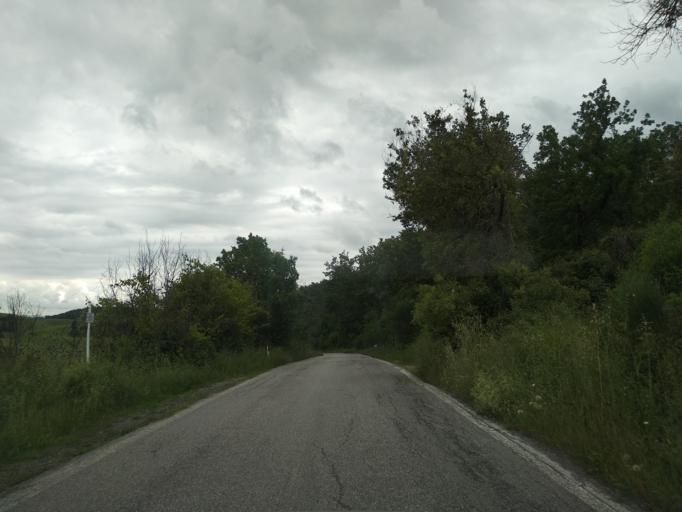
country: IT
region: Tuscany
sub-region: Provincia di Livorno
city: Guasticce
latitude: 43.5664
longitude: 10.4228
